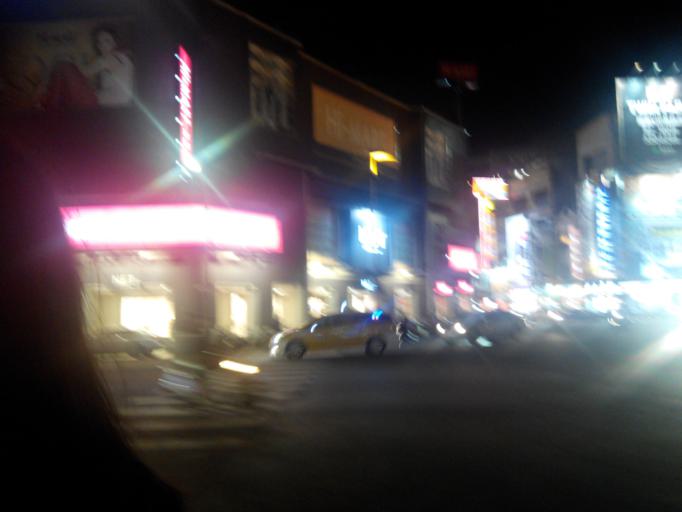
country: TW
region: Taiwan
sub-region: Hsinchu
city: Hsinchu
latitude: 24.7979
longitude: 120.9656
